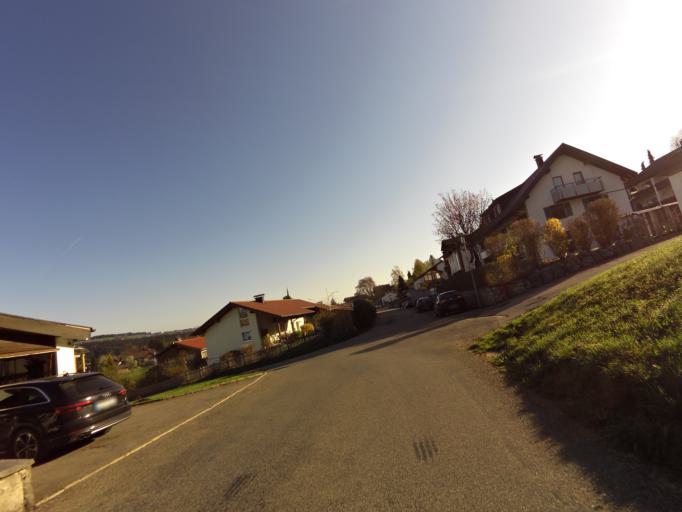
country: DE
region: Bavaria
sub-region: Swabia
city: Weiler-Simmerberg
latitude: 47.5778
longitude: 9.9144
